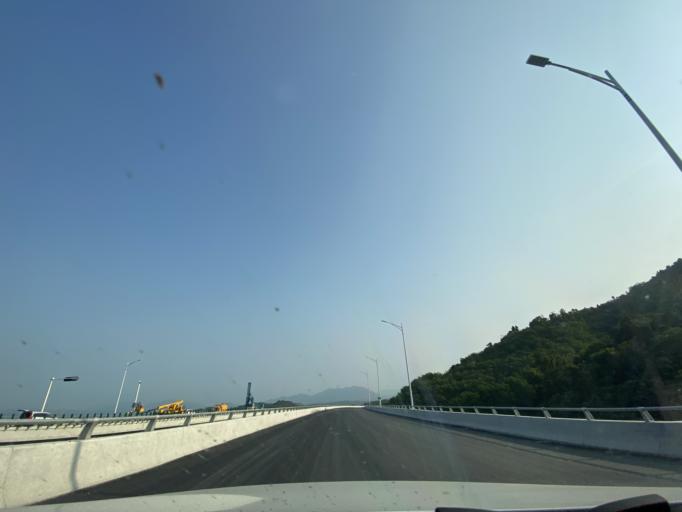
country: CN
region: Hainan
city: Xiangshui
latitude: 18.6621
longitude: 109.6285
